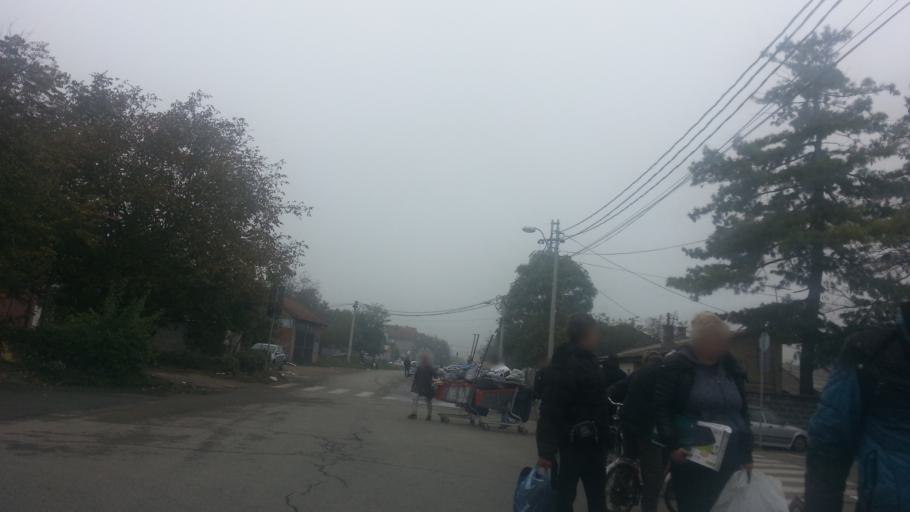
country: RS
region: Central Serbia
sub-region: Belgrade
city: Zemun
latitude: 44.8441
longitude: 20.3771
